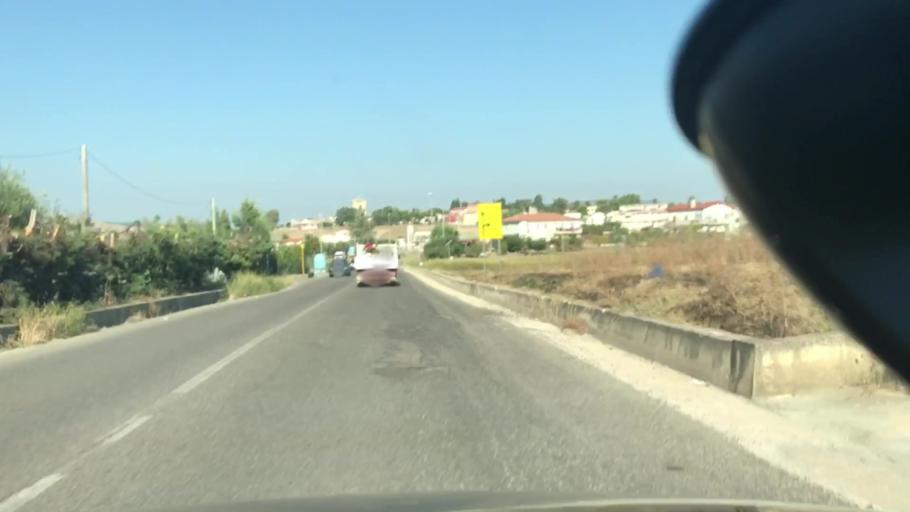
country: IT
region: Basilicate
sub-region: Provincia di Matera
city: La Martella
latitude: 40.6585
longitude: 16.5432
